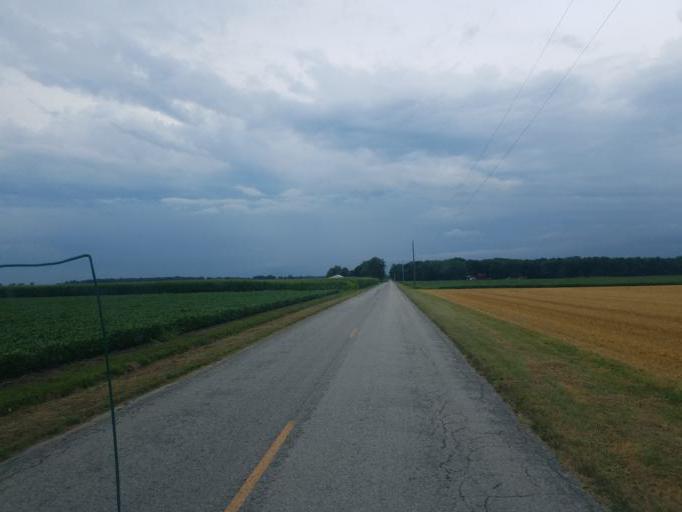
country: US
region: Ohio
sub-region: Defiance County
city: Hicksville
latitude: 41.2373
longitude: -84.7603
